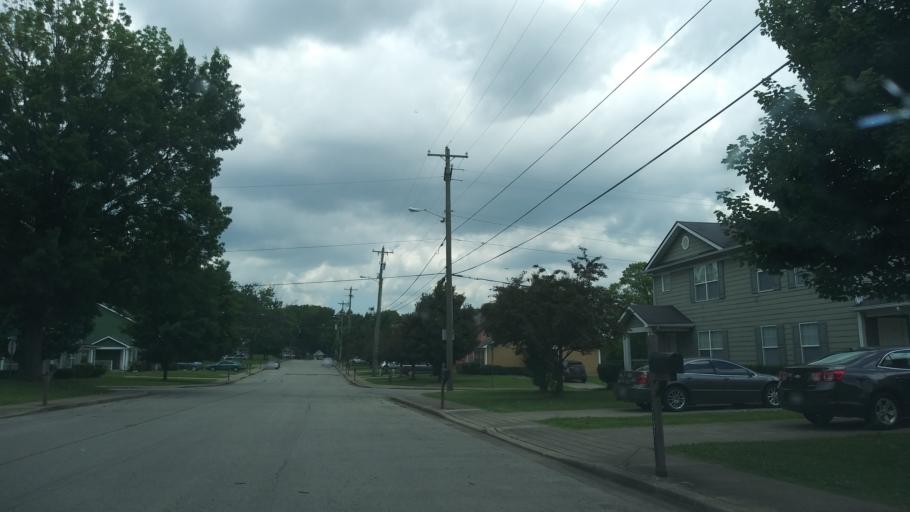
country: US
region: Tennessee
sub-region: Davidson County
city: Nashville
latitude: 36.1294
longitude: -86.7690
